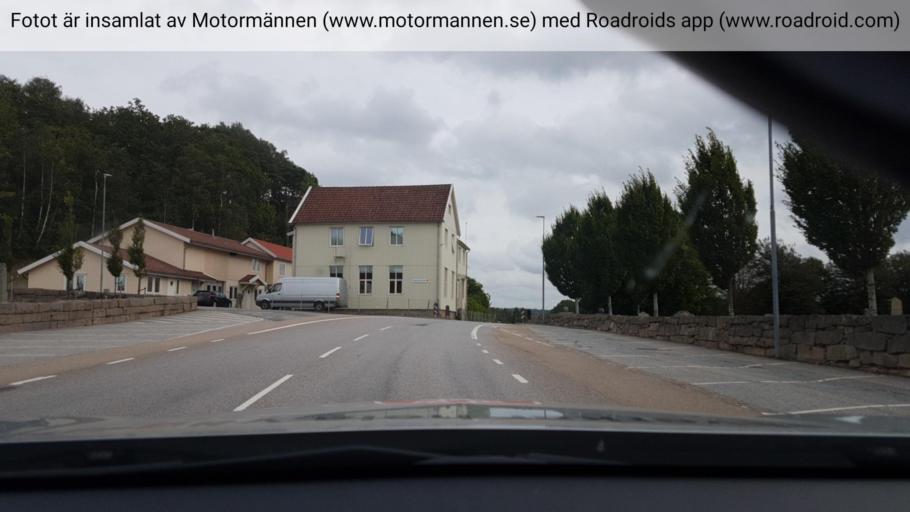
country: SE
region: Vaestra Goetaland
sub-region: Sotenas Kommun
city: Hunnebostrand
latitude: 58.5683
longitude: 11.3676
